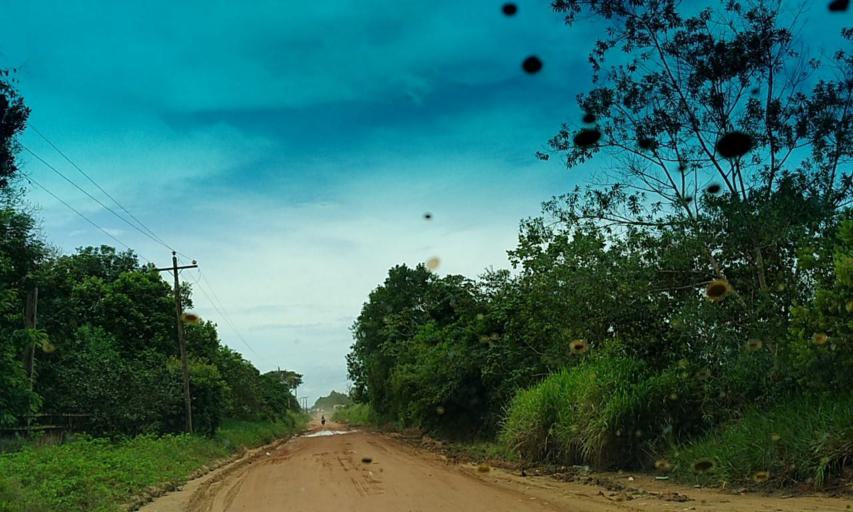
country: BR
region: Para
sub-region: Senador Jose Porfirio
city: Senador Jose Porfirio
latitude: -2.5837
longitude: -51.9395
